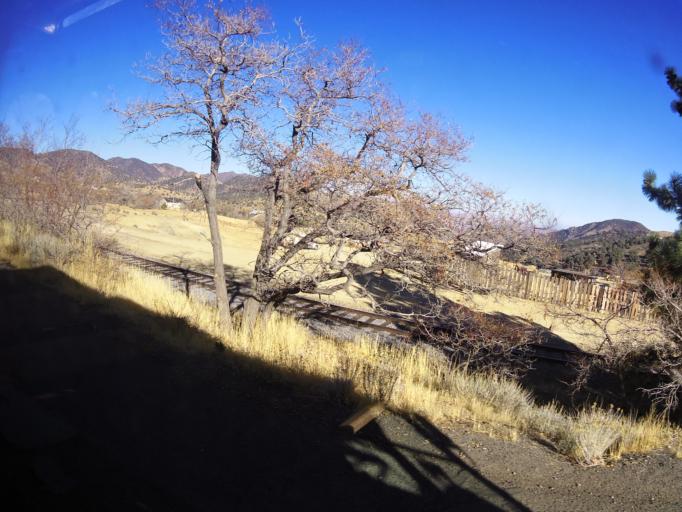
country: US
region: Nevada
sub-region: Storey County
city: Virginia City
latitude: 39.3047
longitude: -119.6498
